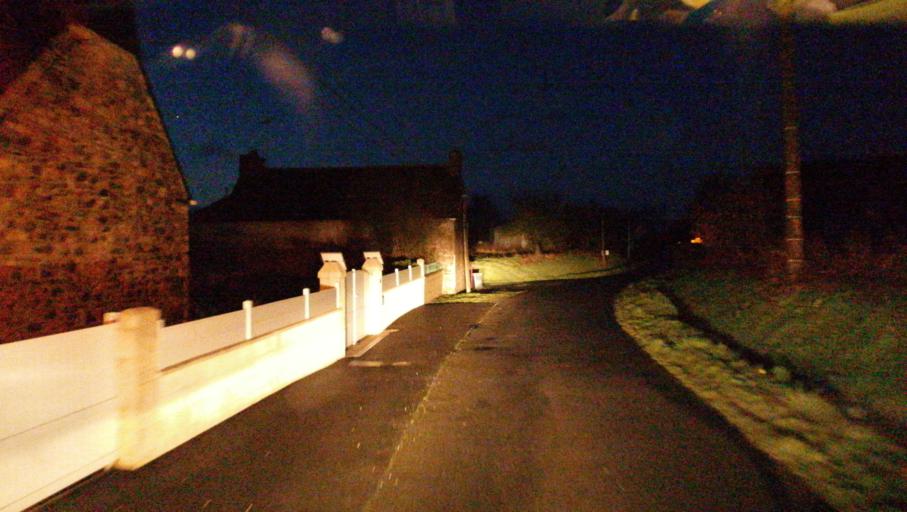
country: FR
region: Brittany
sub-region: Departement des Cotes-d'Armor
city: Pommerit-le-Vicomte
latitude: 48.6584
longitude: -3.0600
